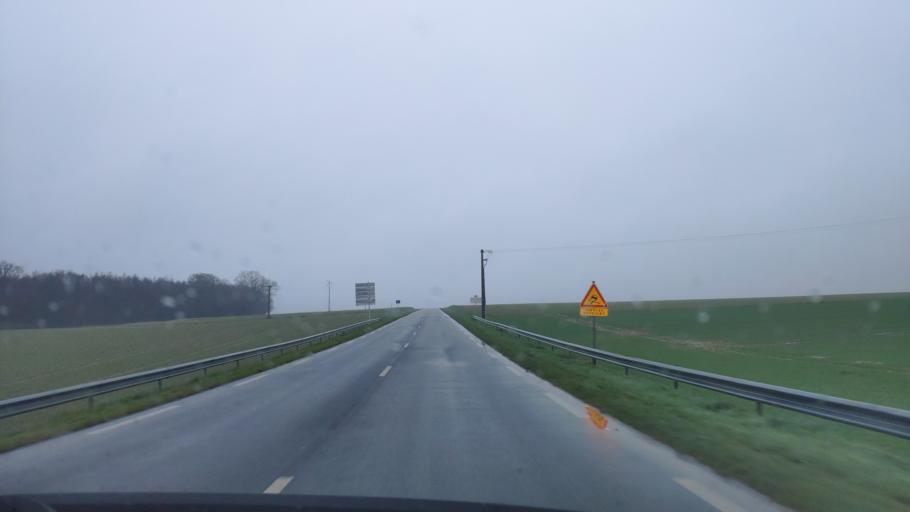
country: FR
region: Haute-Normandie
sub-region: Departement de la Seine-Maritime
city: Doudeville
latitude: 49.7272
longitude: 0.7798
